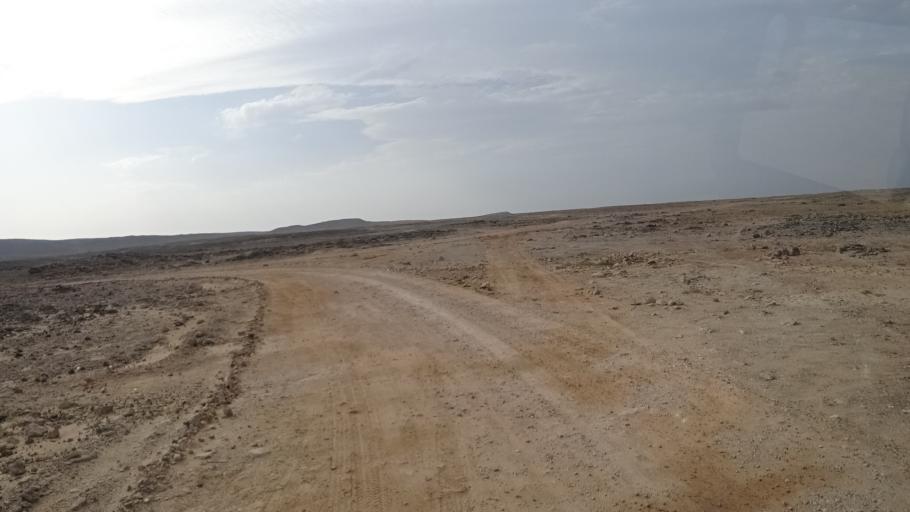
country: OM
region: Ash Sharqiyah
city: Sur
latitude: 22.4523
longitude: 59.8255
